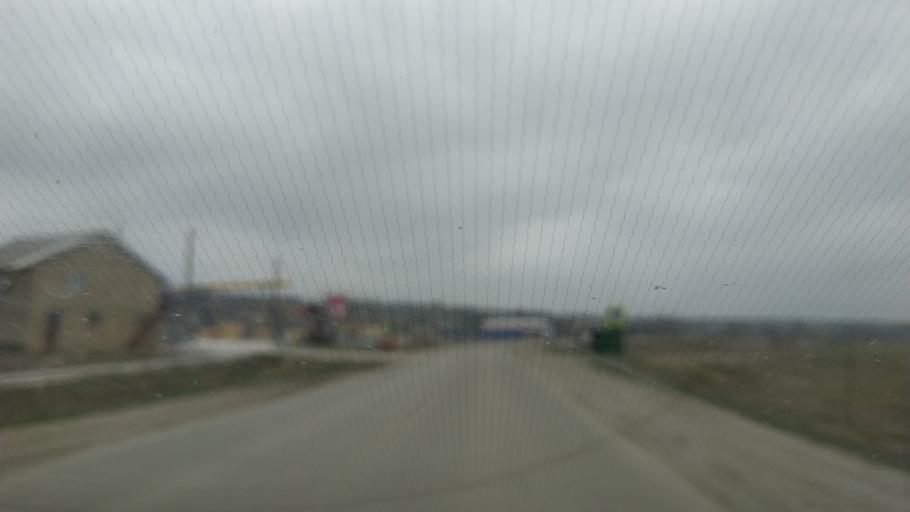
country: MD
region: Gagauzia
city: Comrat
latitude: 46.2923
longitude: 28.6675
